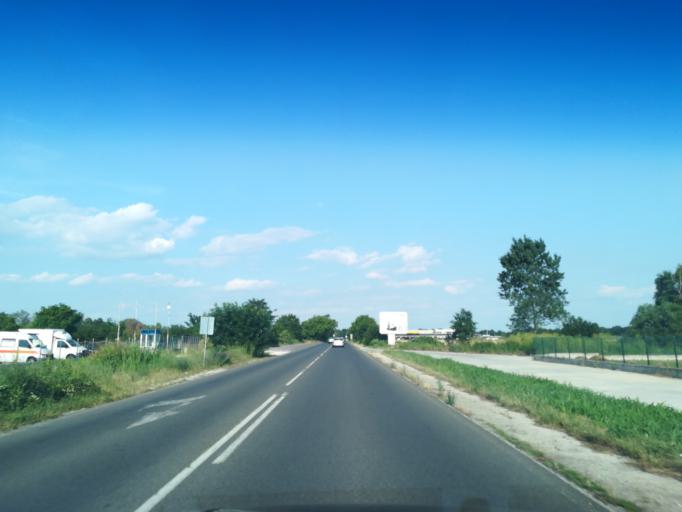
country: BG
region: Plovdiv
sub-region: Obshtina Plovdiv
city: Plovdiv
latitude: 42.1491
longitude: 24.8230
